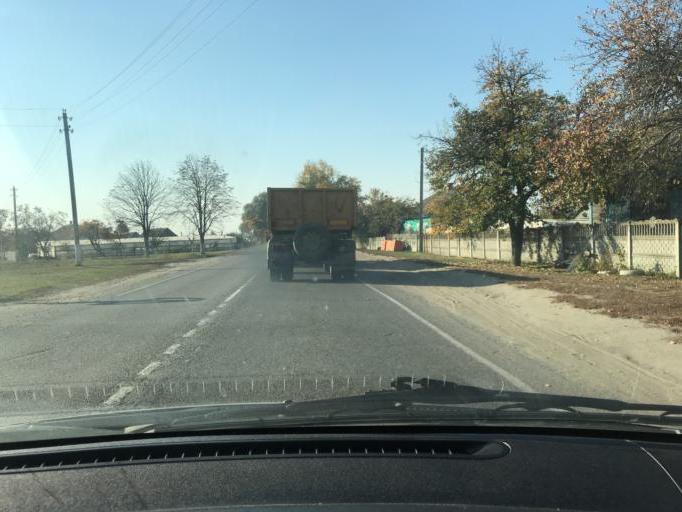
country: BY
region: Brest
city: Davyd-Haradok
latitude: 52.0599
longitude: 27.2803
